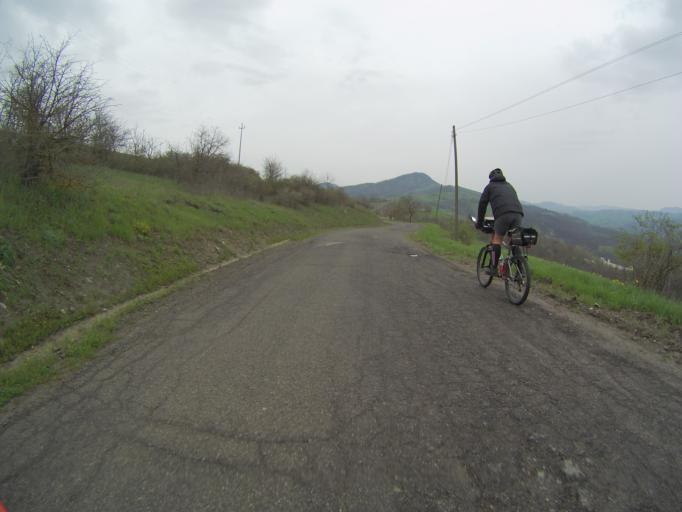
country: IT
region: Emilia-Romagna
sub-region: Provincia di Reggio Emilia
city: Ciano d'Enza
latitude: 44.5429
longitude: 10.4297
